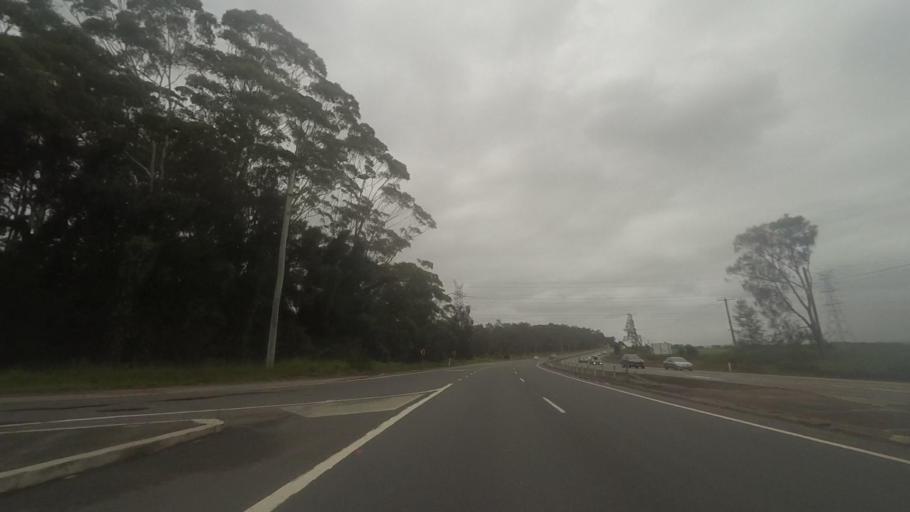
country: AU
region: New South Wales
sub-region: Newcastle
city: Beresfield
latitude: -32.8093
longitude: 151.7105
